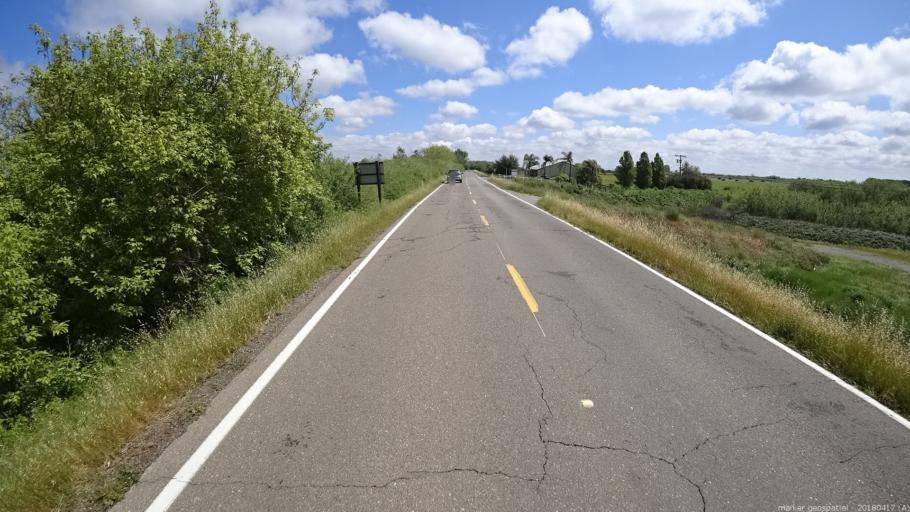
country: US
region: California
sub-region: Sacramento County
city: Walnut Grove
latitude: 38.1917
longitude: -121.5683
